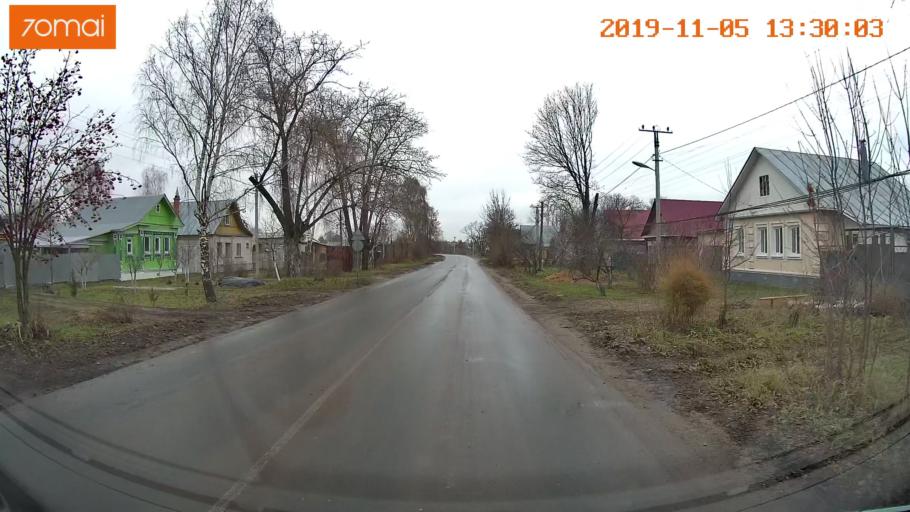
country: RU
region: Ivanovo
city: Shuya
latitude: 56.8644
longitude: 41.3969
